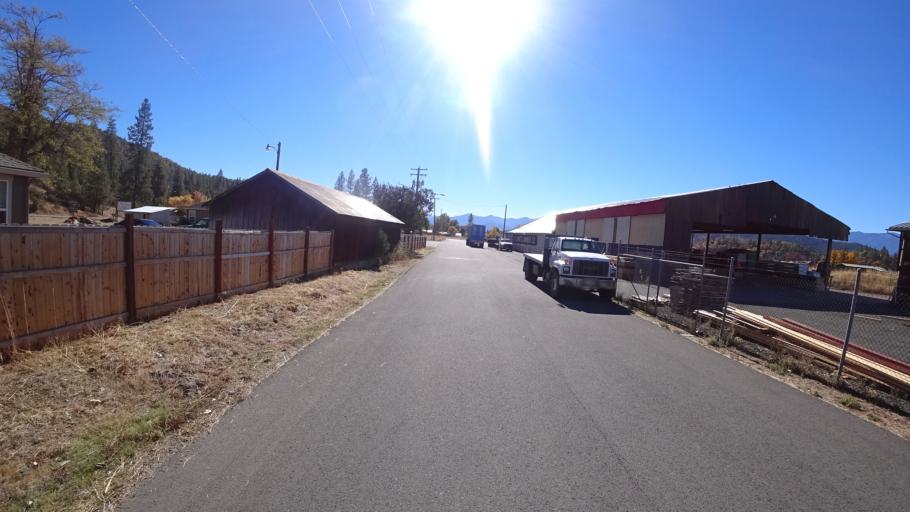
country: US
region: California
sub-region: Siskiyou County
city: Yreka
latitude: 41.6137
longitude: -122.8387
